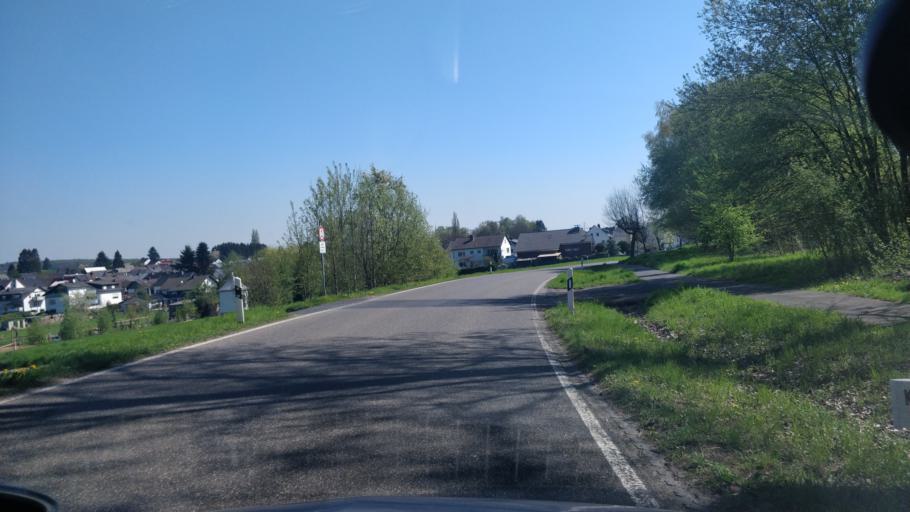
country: DE
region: Hesse
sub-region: Regierungsbezirk Giessen
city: Dehrn
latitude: 50.4554
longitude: 8.0900
